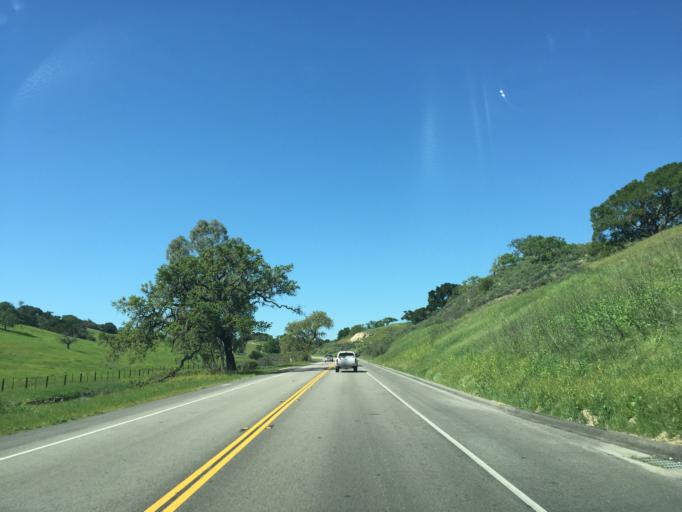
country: US
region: California
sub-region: Santa Barbara County
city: Los Olivos
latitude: 34.6719
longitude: -120.1282
